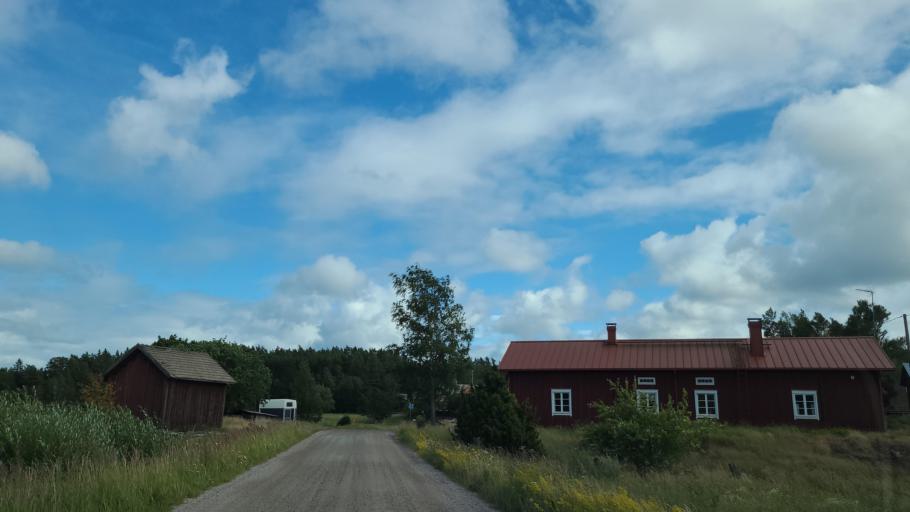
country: FI
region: Varsinais-Suomi
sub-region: Aboland-Turunmaa
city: Nagu
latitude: 60.1519
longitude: 21.7584
